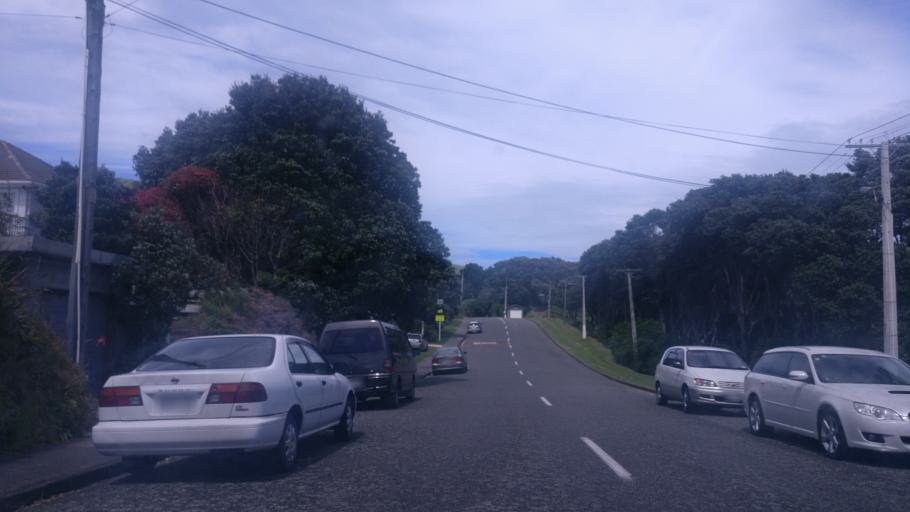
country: NZ
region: Wellington
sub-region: Kapiti Coast District
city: Paraparaumu
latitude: -40.9797
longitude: 174.9580
